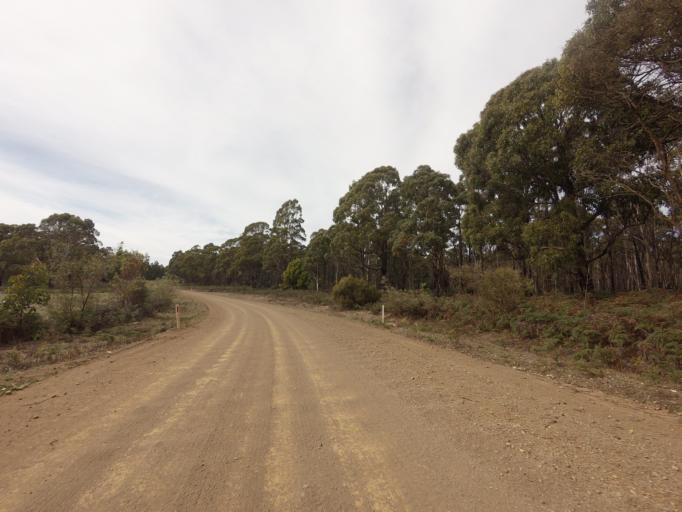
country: AU
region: Tasmania
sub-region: Sorell
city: Sorell
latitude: -42.5001
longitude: 147.6309
